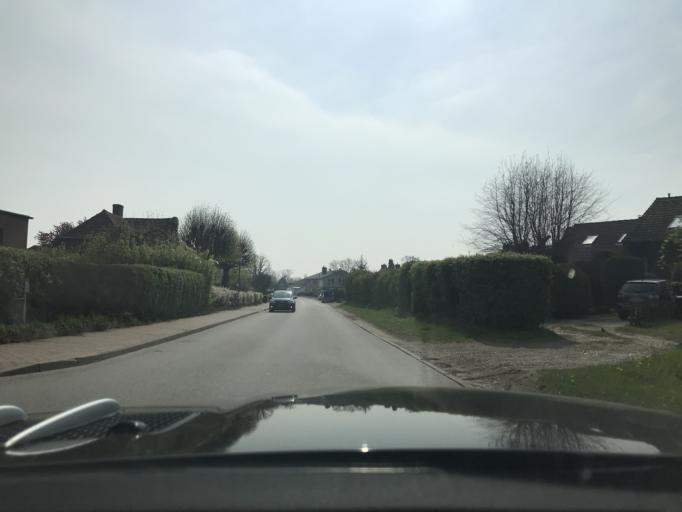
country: DE
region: Schleswig-Holstein
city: Gromitz
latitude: 54.1682
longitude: 10.9789
